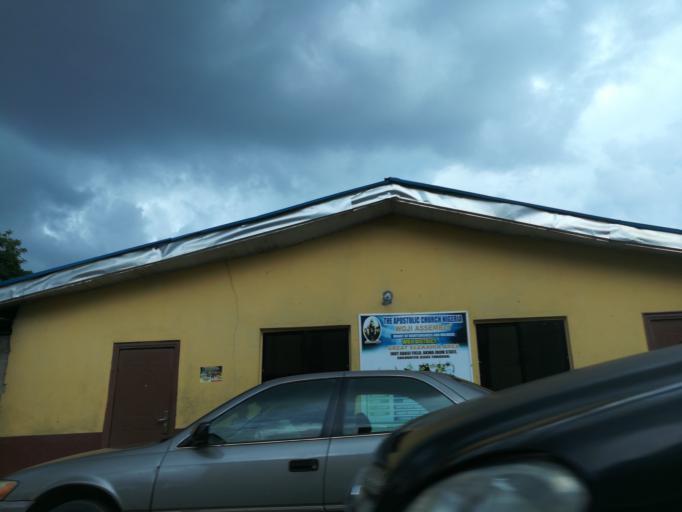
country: NG
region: Rivers
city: Port Harcourt
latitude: 4.8190
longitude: 7.0671
